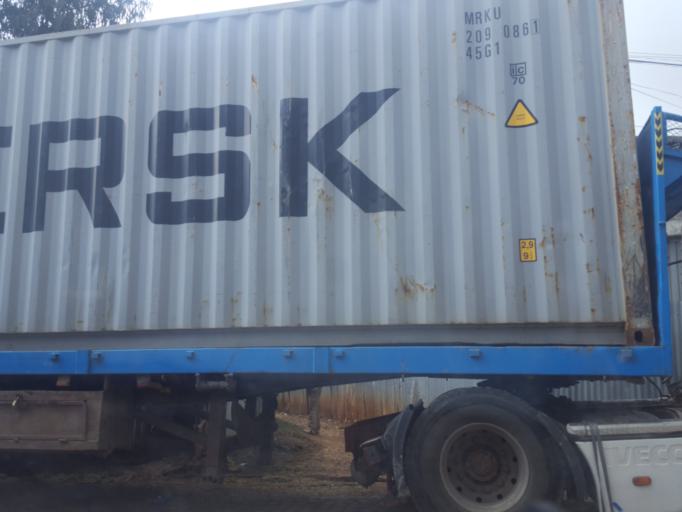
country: ET
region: Adis Abeba
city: Addis Ababa
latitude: 9.0670
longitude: 38.7284
